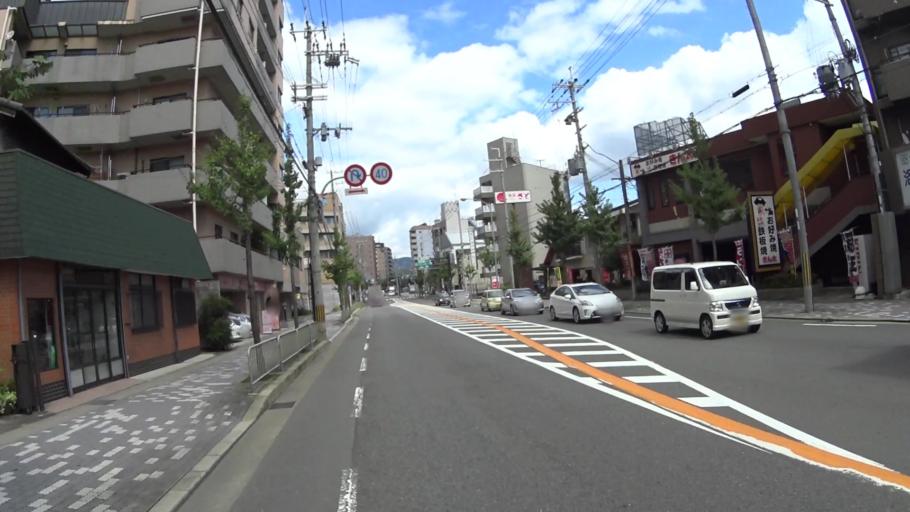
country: JP
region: Shiga Prefecture
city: Otsu-shi
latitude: 34.9703
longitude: 135.8137
